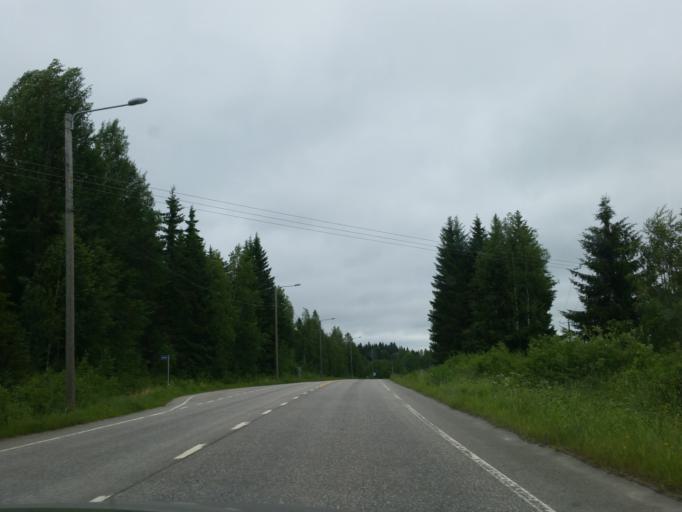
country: FI
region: Northern Savo
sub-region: Koillis-Savo
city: Kaavi
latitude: 62.9742
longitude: 28.4987
